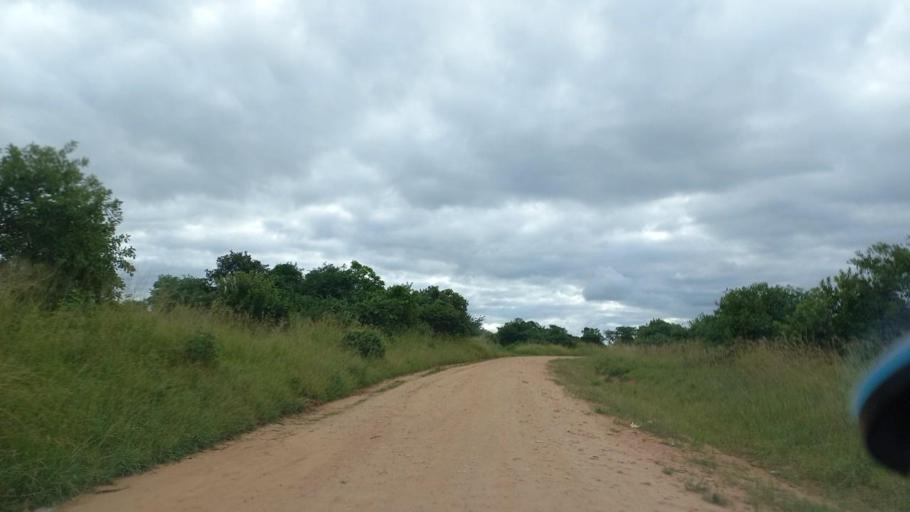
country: ZM
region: Lusaka
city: Chongwe
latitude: -15.4516
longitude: 28.8323
